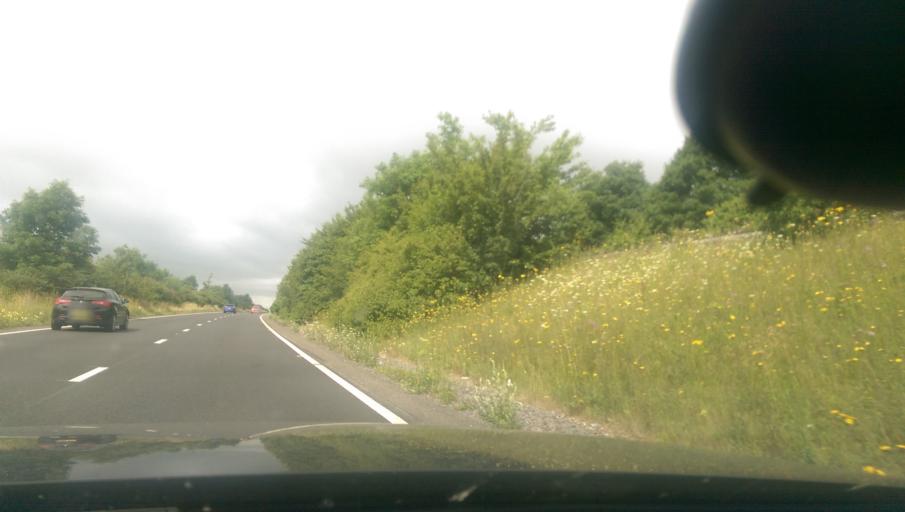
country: GB
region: England
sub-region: Wiltshire
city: Allington
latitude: 51.1810
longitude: -1.7173
